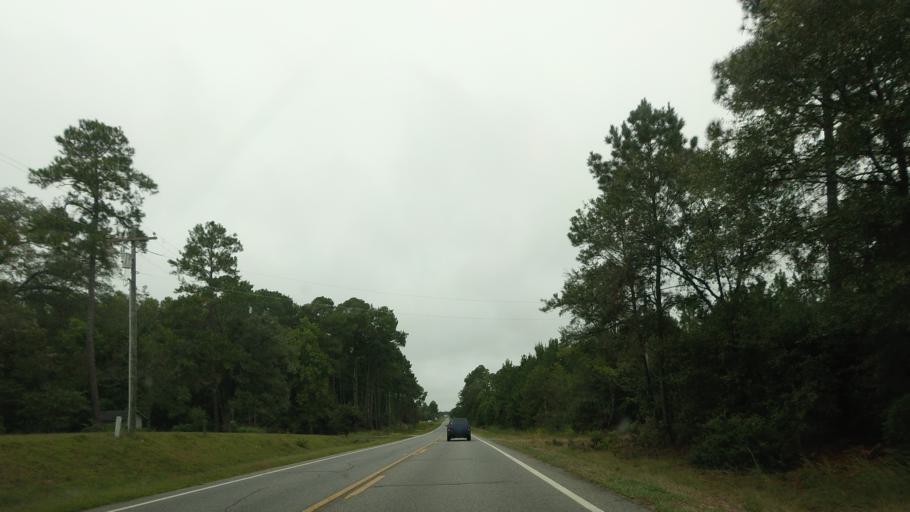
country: US
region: Georgia
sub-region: Irwin County
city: Ocilla
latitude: 31.5616
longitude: -83.2529
